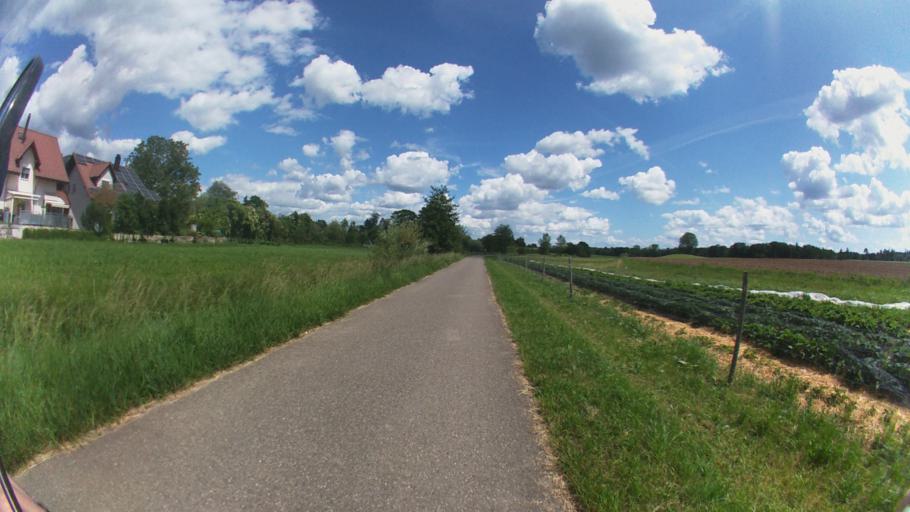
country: CH
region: Zurich
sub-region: Bezirk Dielsdorf
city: Regensdorf
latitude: 47.4415
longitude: 8.4840
